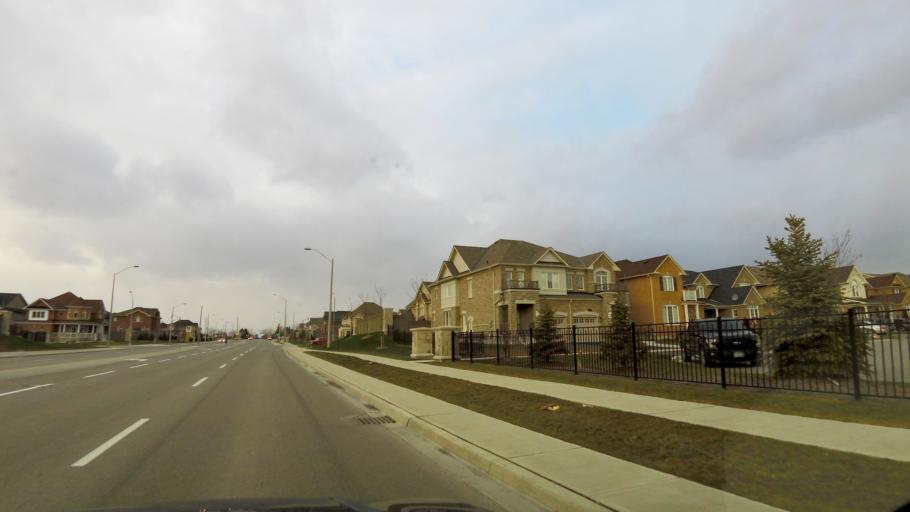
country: CA
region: Ontario
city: Brampton
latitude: 43.7987
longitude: -79.6753
